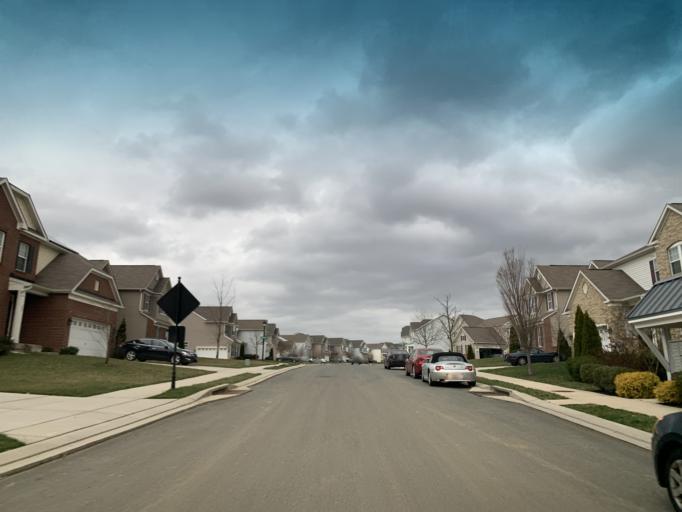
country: US
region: Maryland
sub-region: Harford County
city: Perryman
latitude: 39.4948
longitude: -76.2054
